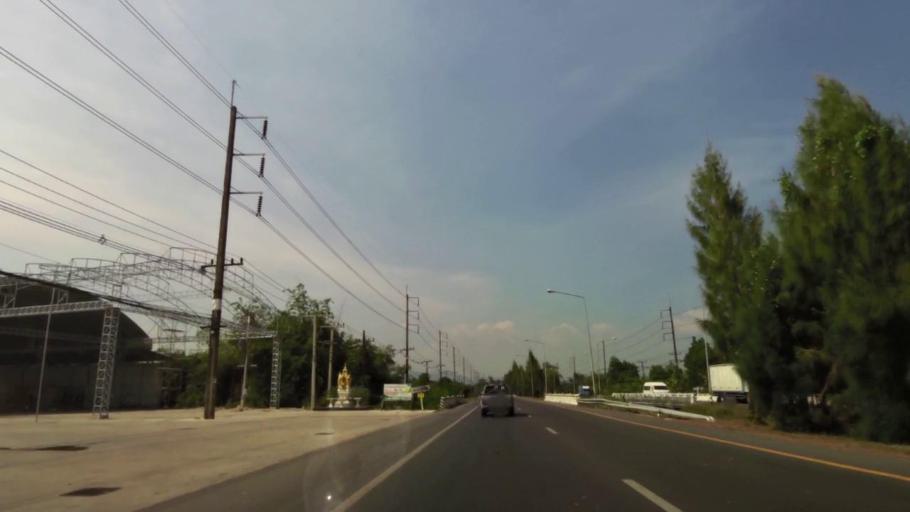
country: TH
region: Chanthaburi
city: Chanthaburi
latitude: 12.6390
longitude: 102.1350
